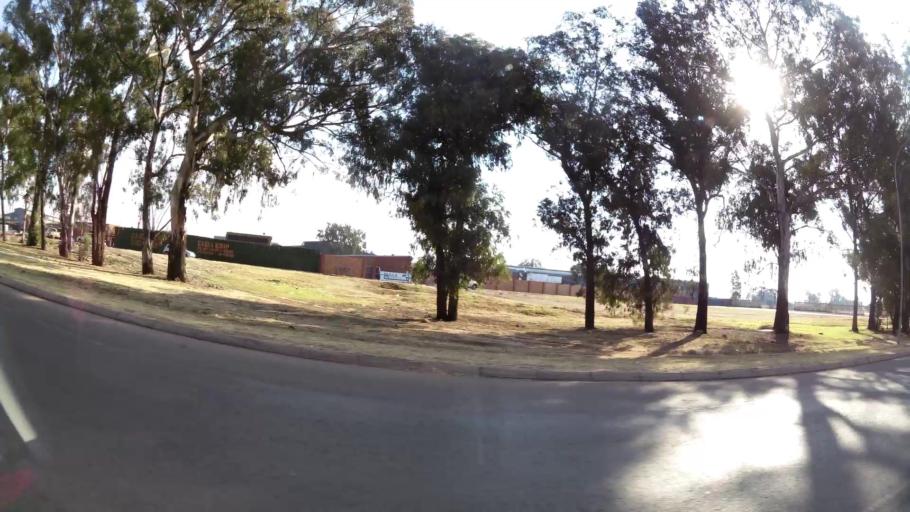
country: ZA
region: Gauteng
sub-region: Ekurhuleni Metropolitan Municipality
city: Tembisa
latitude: -25.9480
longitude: 28.2333
